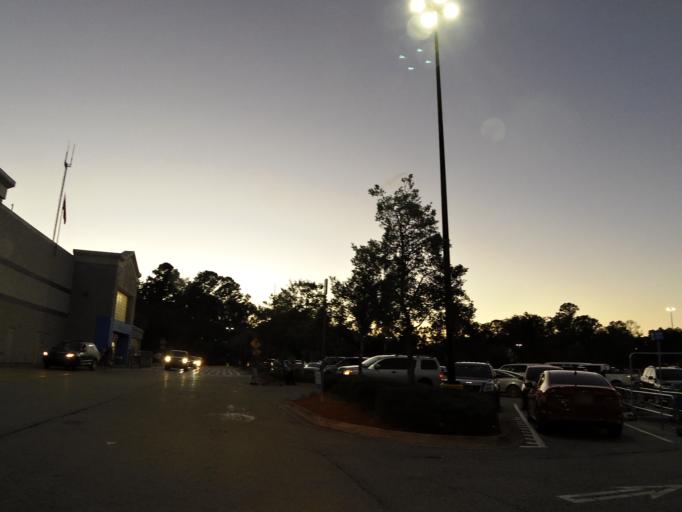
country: US
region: Florida
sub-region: Duval County
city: Jacksonville
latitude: 30.2841
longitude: -81.5627
